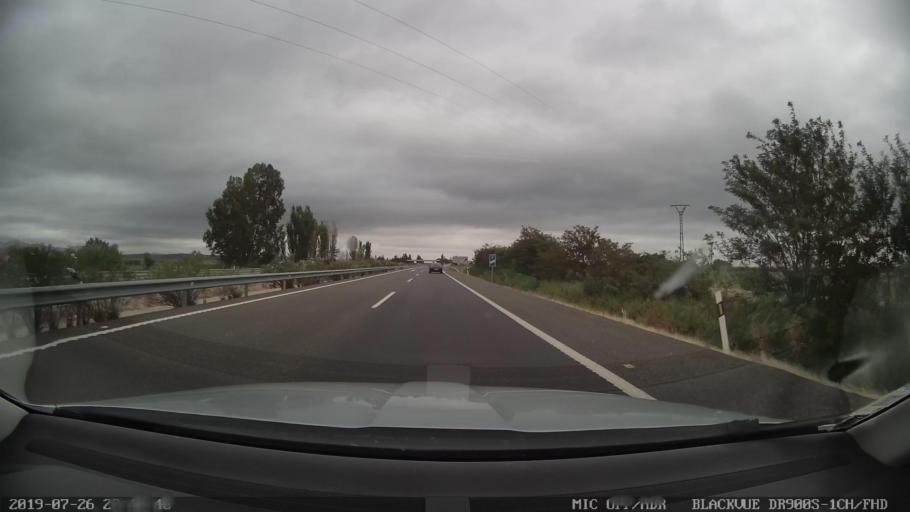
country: ES
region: Extremadura
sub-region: Provincia de Caceres
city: Almoharin
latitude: 39.0998
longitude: -6.0058
